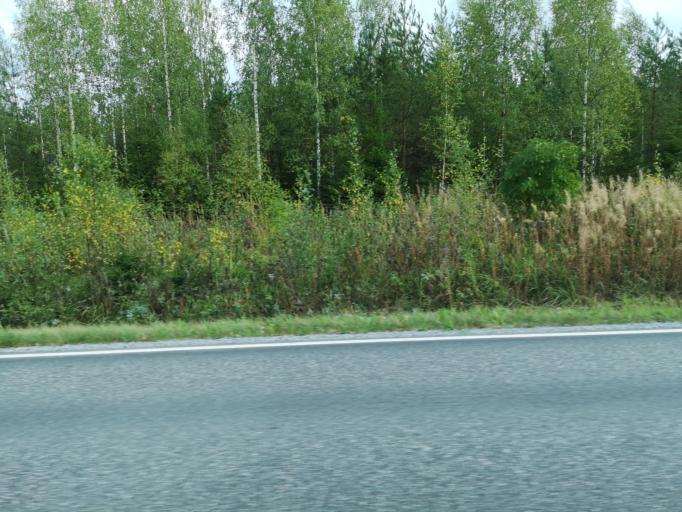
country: FI
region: Central Finland
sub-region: Jyvaeskylae
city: Hankasalmi
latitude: 62.3562
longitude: 26.4538
